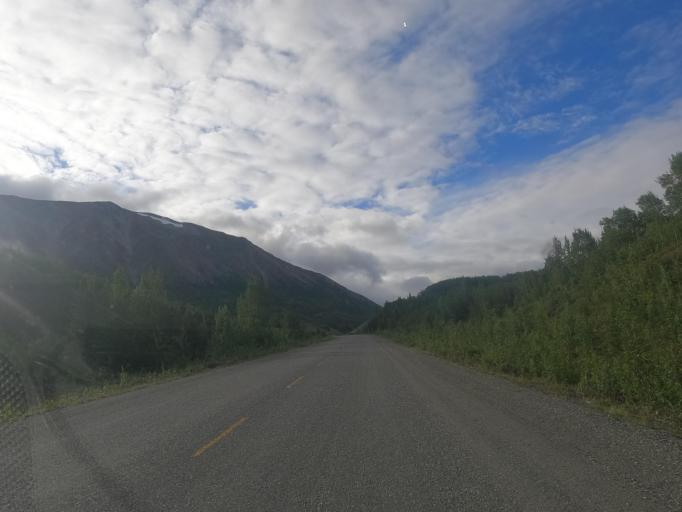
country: CA
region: Yukon
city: Haines Junction
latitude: 60.1054
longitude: -136.9198
